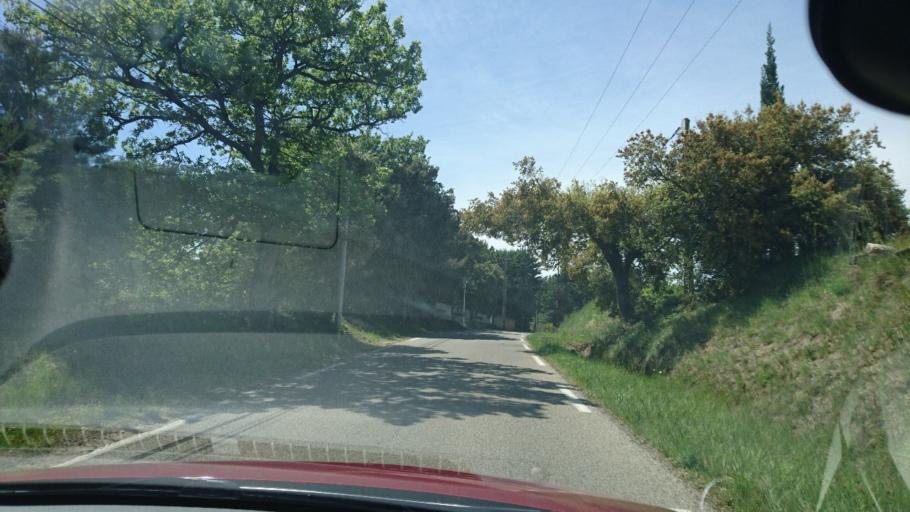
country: FR
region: Provence-Alpes-Cote d'Azur
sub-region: Departement du Vaucluse
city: Bedoin
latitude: 44.1303
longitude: 5.1735
